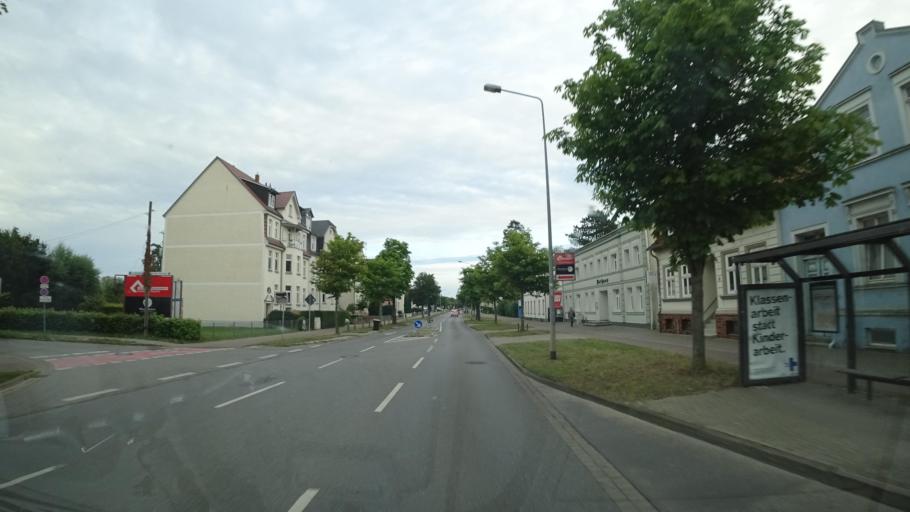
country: DE
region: Mecklenburg-Vorpommern
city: Greifswald
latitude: 54.0951
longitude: 13.3958
